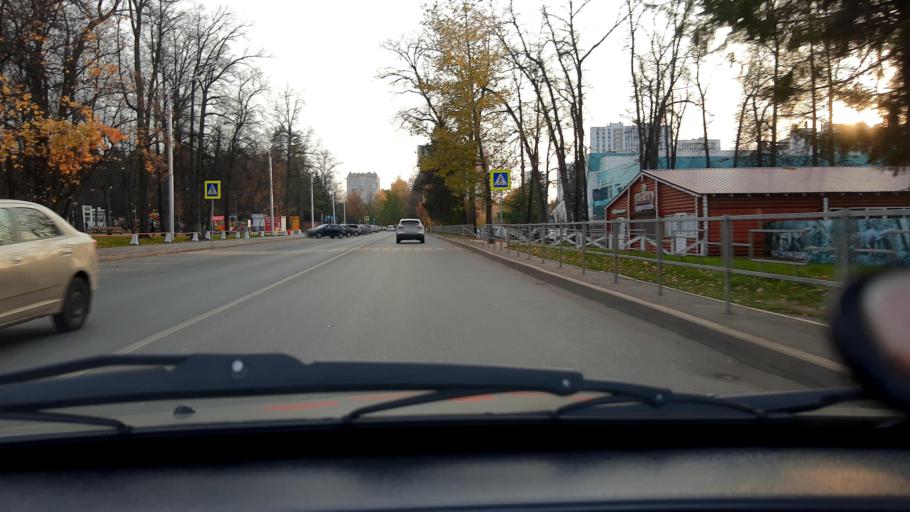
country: RU
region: Bashkortostan
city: Ufa
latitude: 54.7746
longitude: 56.0191
